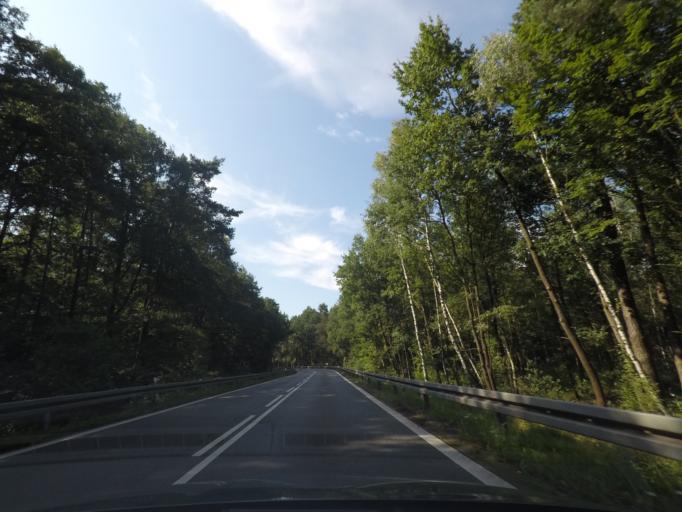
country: PL
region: Silesian Voivodeship
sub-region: Powiat pszczynski
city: Radostowice
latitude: 50.0191
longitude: 18.8480
